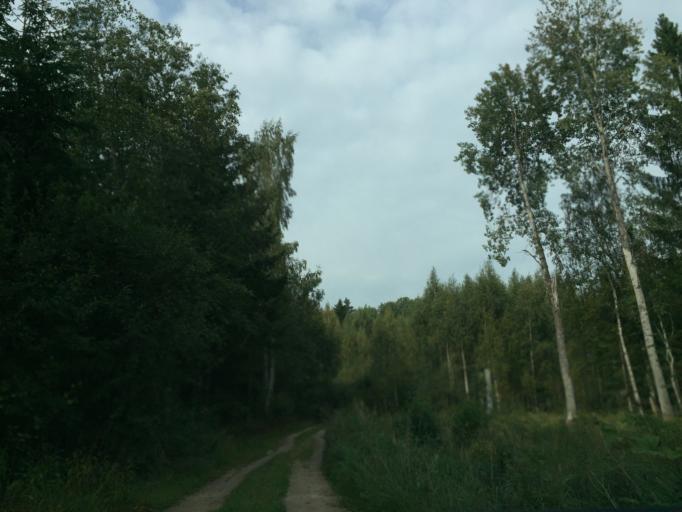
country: LV
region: Ikskile
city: Ikskile
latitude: 56.7591
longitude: 24.4751
